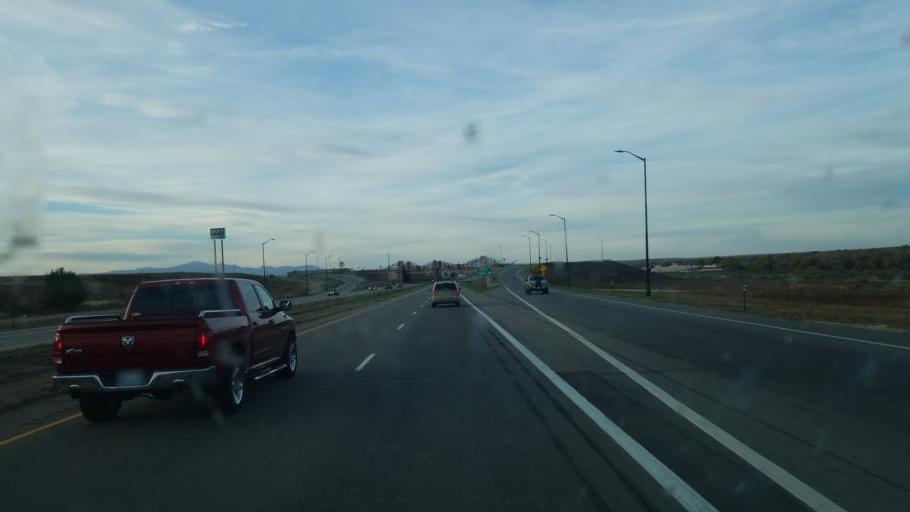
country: US
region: Colorado
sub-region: Pueblo County
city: Pueblo
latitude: 38.3341
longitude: -104.6184
